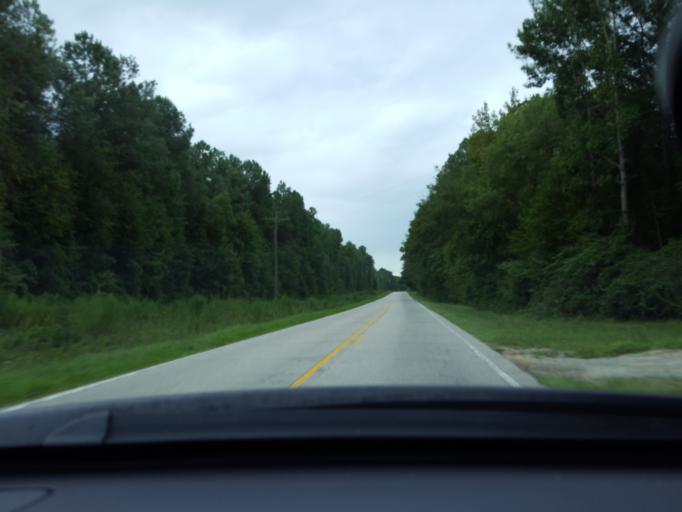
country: US
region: North Carolina
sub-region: Sampson County
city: Clinton
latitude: 34.7846
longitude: -78.3228
